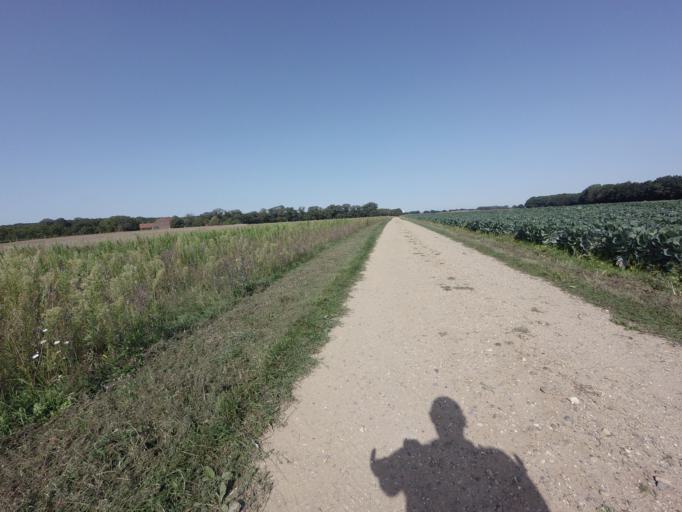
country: NL
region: Limburg
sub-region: Gemeente Roerdalen
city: Sint Odilienberg
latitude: 51.1490
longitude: 5.9823
